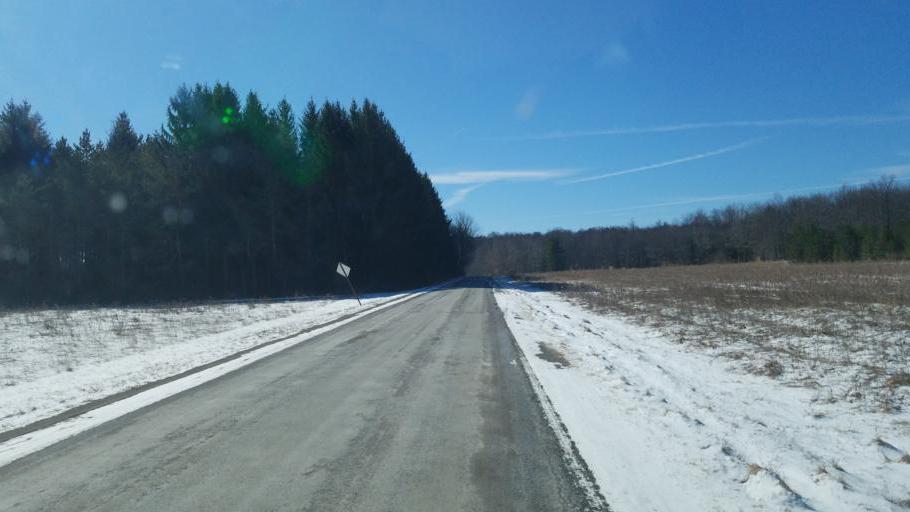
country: US
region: New York
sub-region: Allegany County
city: Wellsville
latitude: 42.0562
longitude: -78.0089
